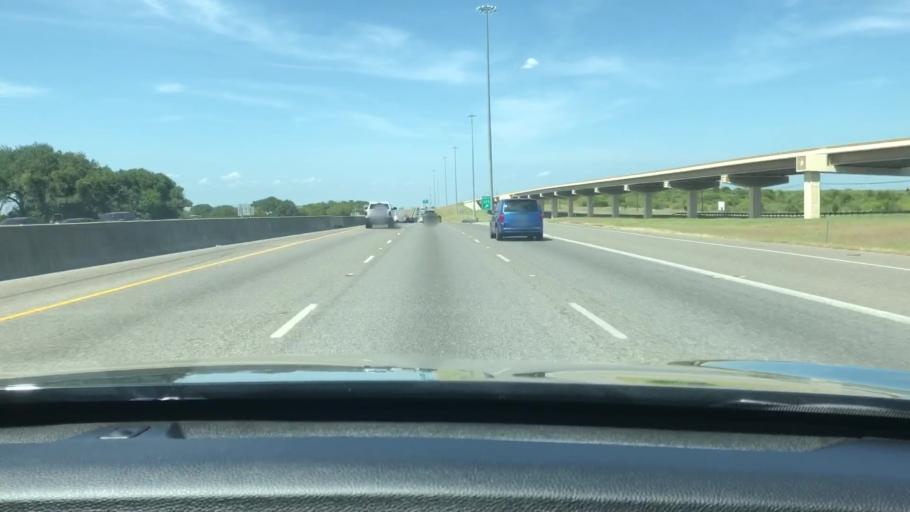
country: US
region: Texas
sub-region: Travis County
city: Onion Creek
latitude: 30.1141
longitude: -97.8061
